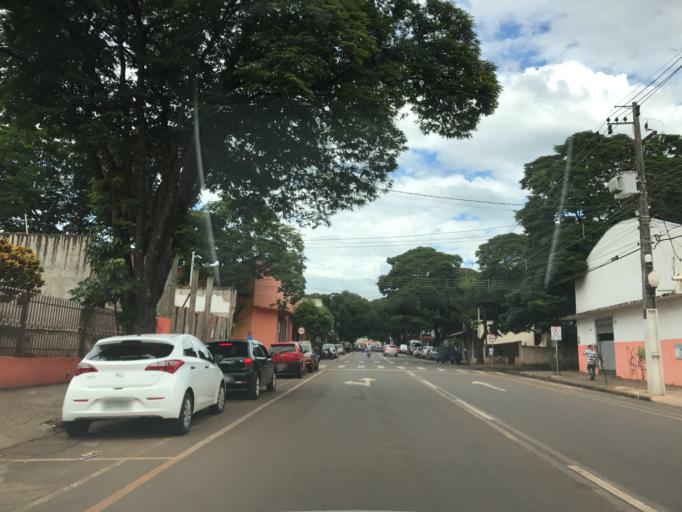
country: BR
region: Parana
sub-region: Sarandi
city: Sarandi
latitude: -23.4370
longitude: -51.8713
